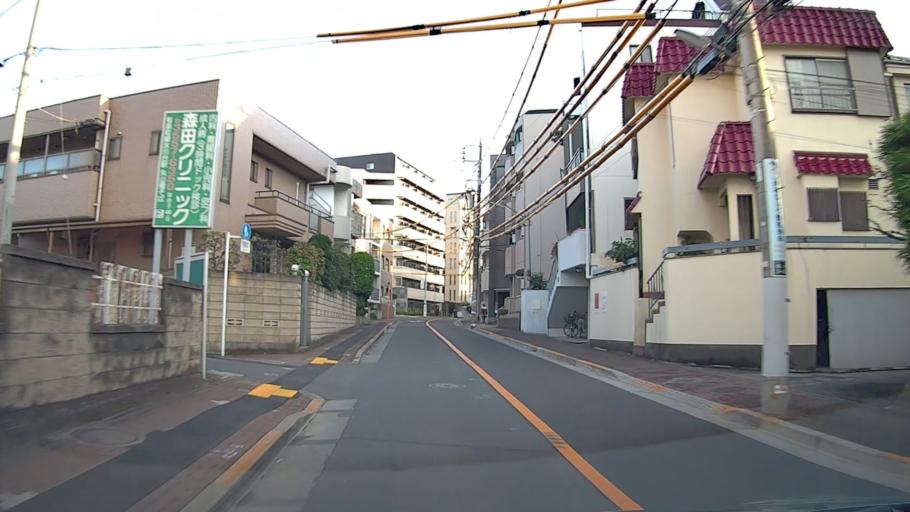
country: JP
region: Saitama
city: Wako
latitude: 35.7465
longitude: 139.6671
